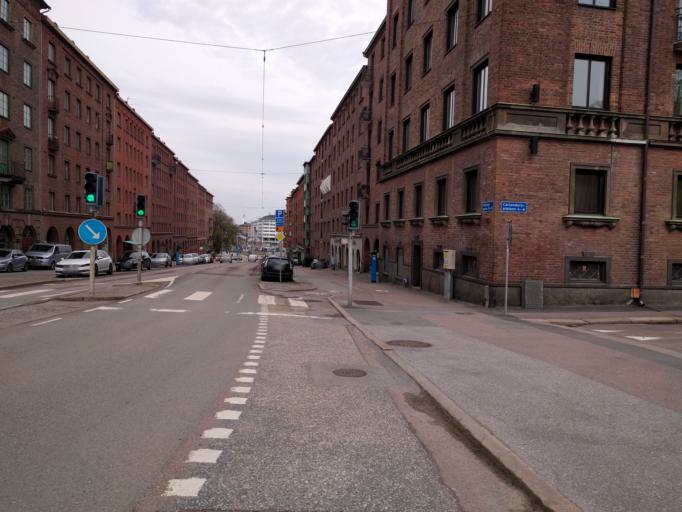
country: SE
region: Vaestra Goetaland
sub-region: Goteborg
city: Goeteborg
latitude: 57.6934
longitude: 11.9874
